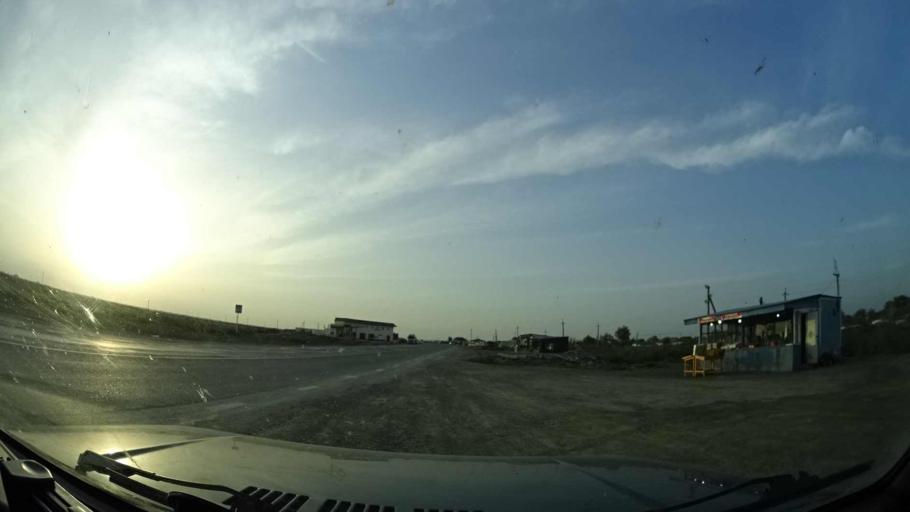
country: RU
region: Dagestan
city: Kochubey
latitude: 44.2355
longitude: 46.5873
